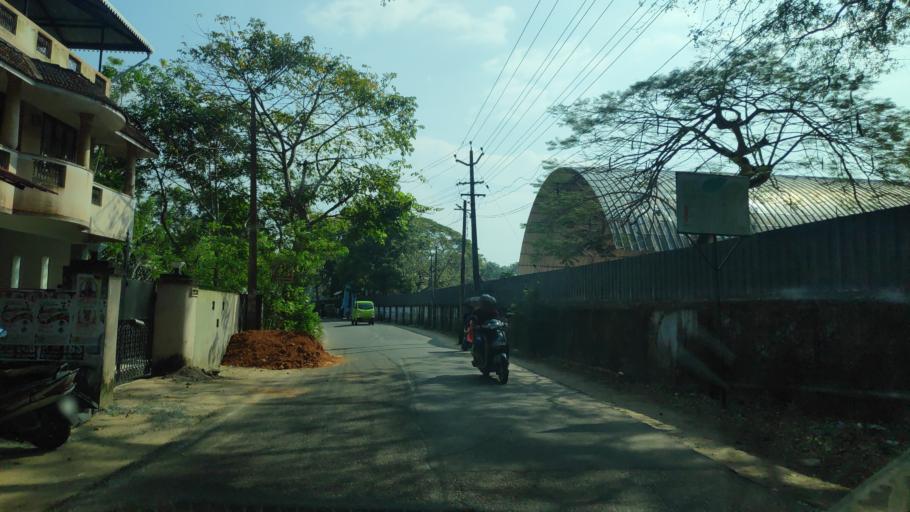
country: IN
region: Kerala
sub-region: Alappuzha
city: Alleppey
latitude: 9.5667
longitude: 76.3087
